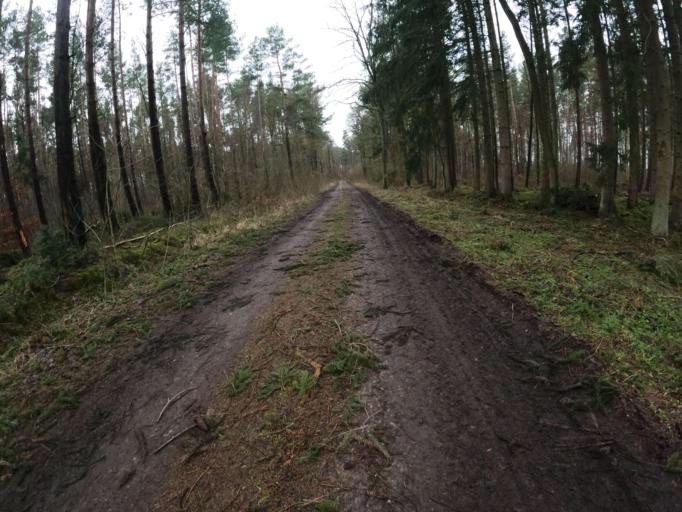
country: PL
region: West Pomeranian Voivodeship
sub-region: Powiat slawienski
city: Darlowo
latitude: 54.4181
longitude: 16.4690
